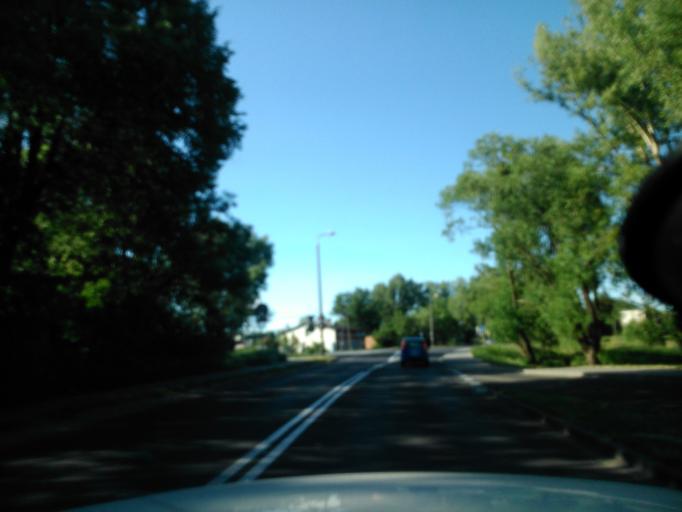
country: PL
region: Kujawsko-Pomorskie
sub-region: Powiat torunski
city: Lubicz Dolny
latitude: 53.0459
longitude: 18.7010
